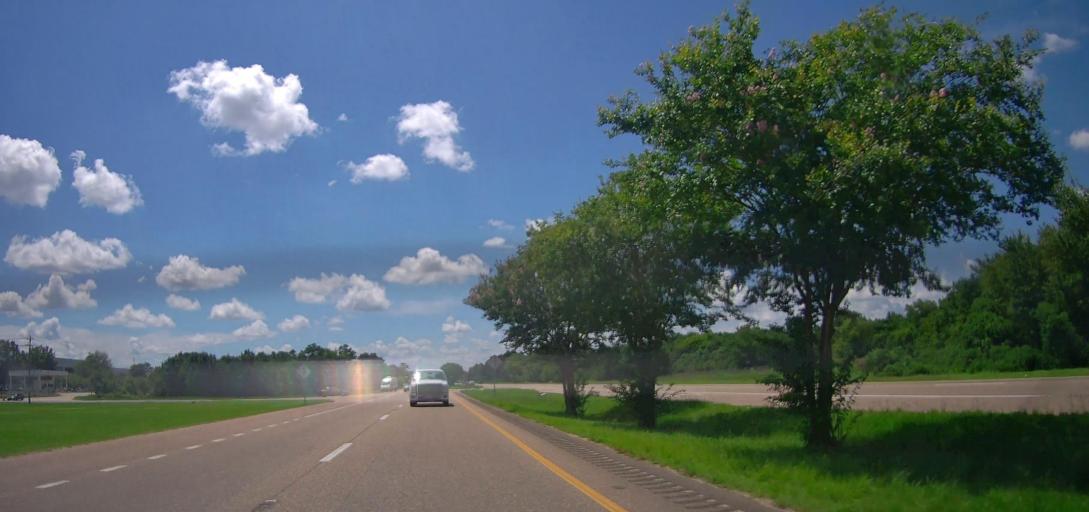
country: US
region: Alabama
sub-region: Montgomery County
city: Montgomery
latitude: 32.4224
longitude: -86.2581
